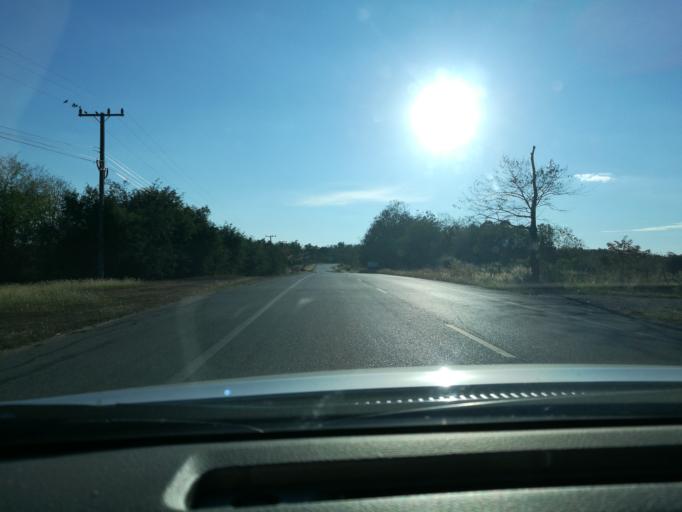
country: TH
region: Phitsanulok
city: Nakhon Thai
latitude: 17.0729
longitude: 100.8509
